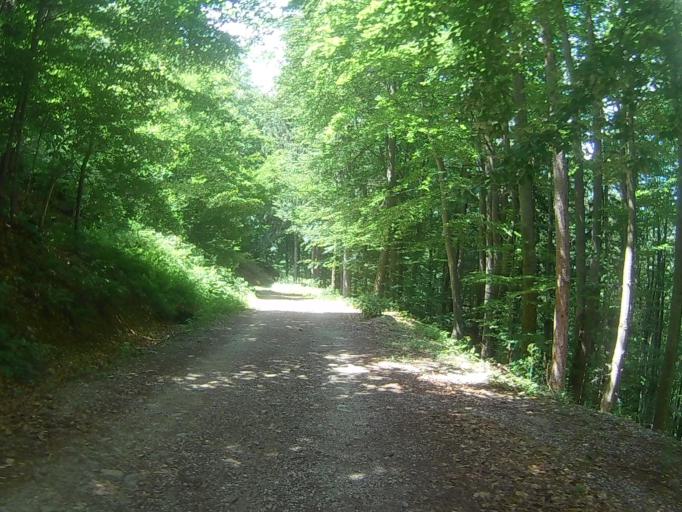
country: SI
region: Selnica ob Dravi
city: Selnica ob Dravi
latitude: 46.5231
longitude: 15.4917
